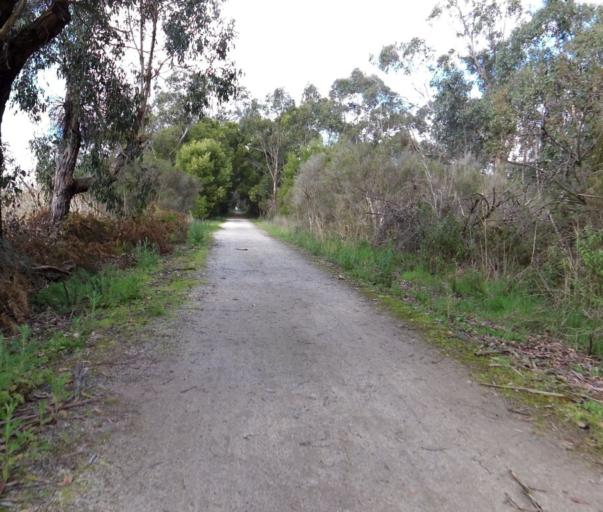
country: AU
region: Victoria
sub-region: Baw Baw
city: Warragul
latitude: -38.5792
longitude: 146.0316
